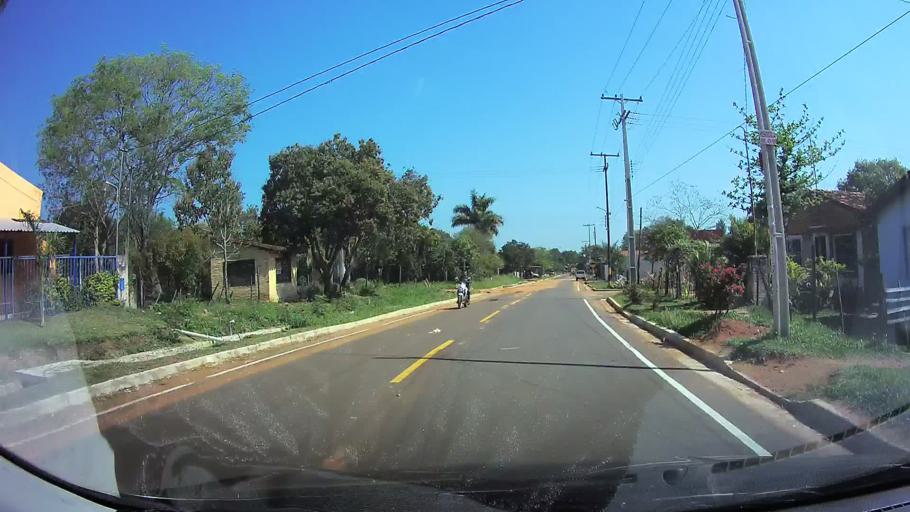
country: PY
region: Central
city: Limpio
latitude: -25.2276
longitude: -57.4892
